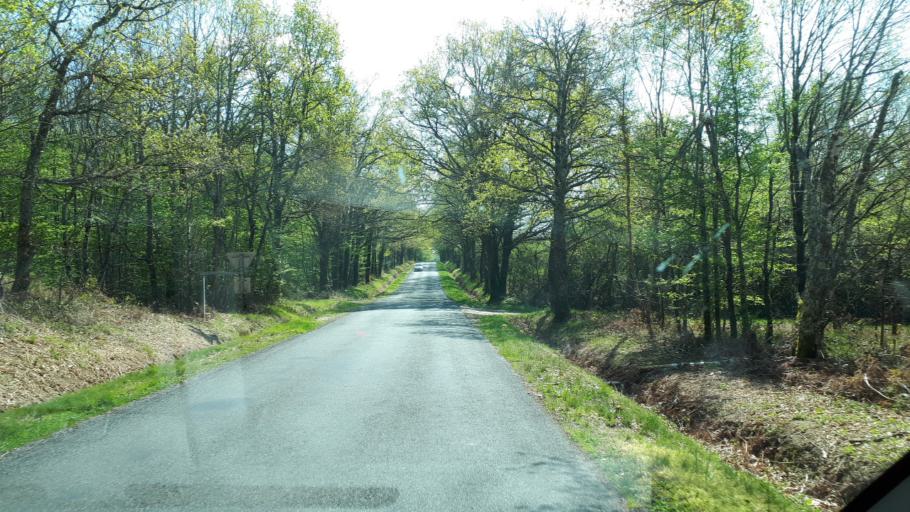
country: FR
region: Centre
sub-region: Departement du Cher
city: Neuvy-sur-Barangeon
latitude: 47.3249
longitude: 2.3331
